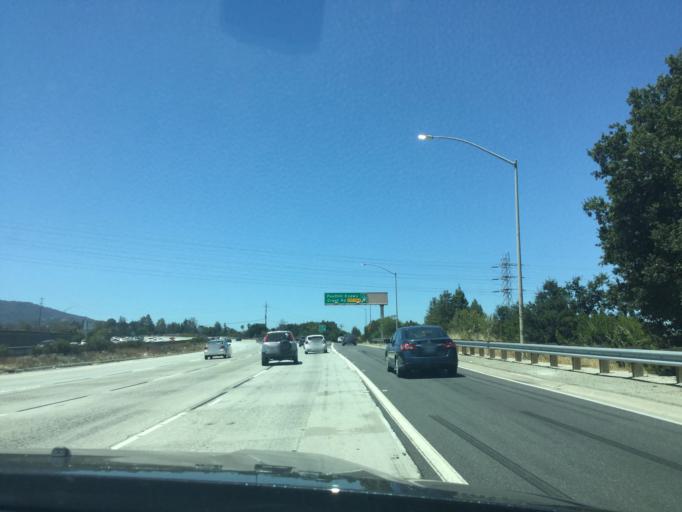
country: US
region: California
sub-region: Santa Clara County
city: Cupertino
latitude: 37.3338
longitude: -122.0638
